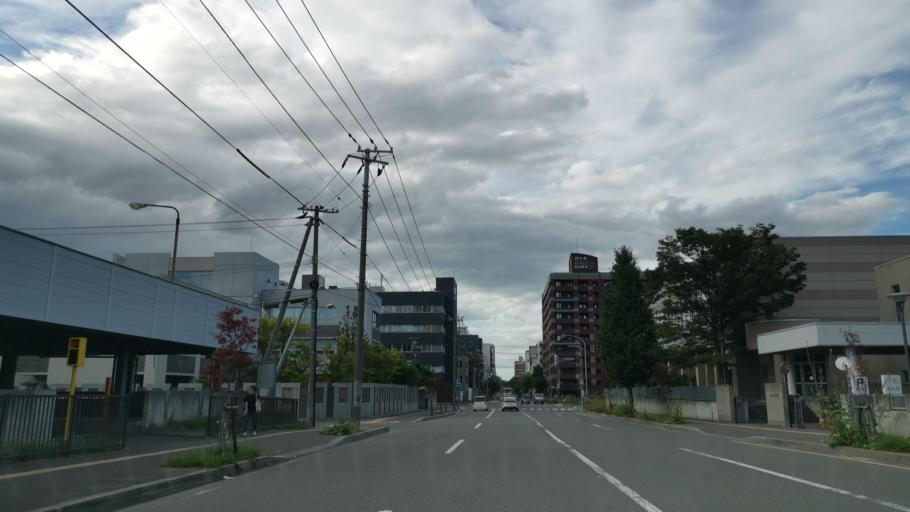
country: JP
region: Hokkaido
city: Sapporo
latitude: 43.0617
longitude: 141.3389
